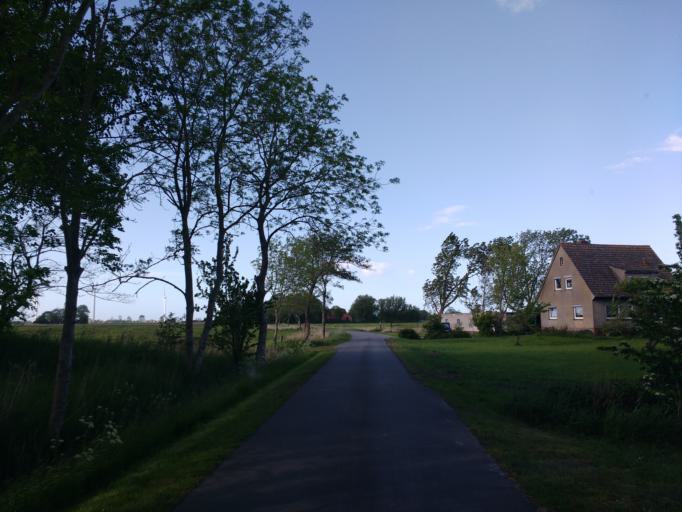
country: DE
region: Lower Saxony
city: Schillig
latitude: 53.6807
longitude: 7.9319
